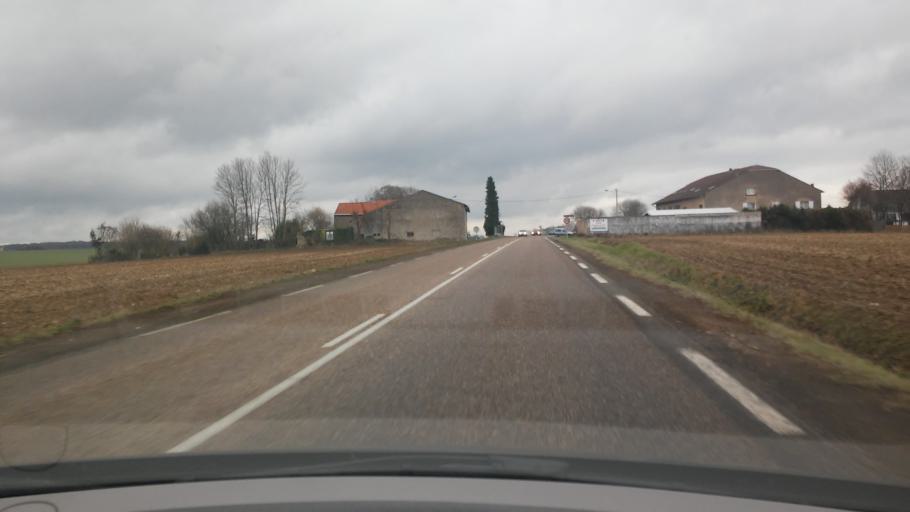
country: FR
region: Lorraine
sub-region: Departement de la Moselle
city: Retonfey
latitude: 49.1160
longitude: 6.3008
